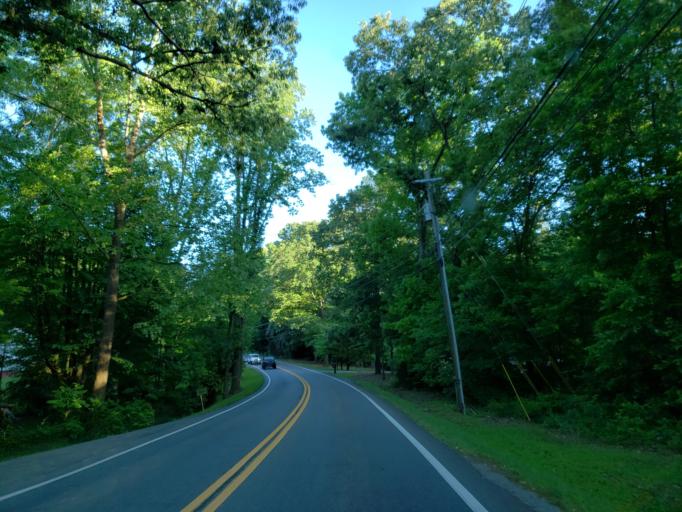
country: US
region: Georgia
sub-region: Cherokee County
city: Canton
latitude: 34.2107
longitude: -84.5274
